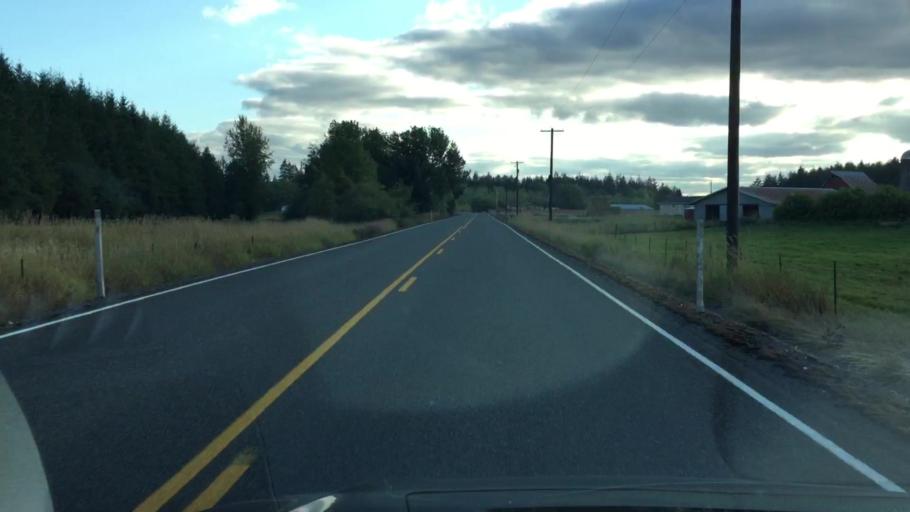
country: US
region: Washington
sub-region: Lewis County
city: Napavine
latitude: 46.5161
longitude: -122.7426
